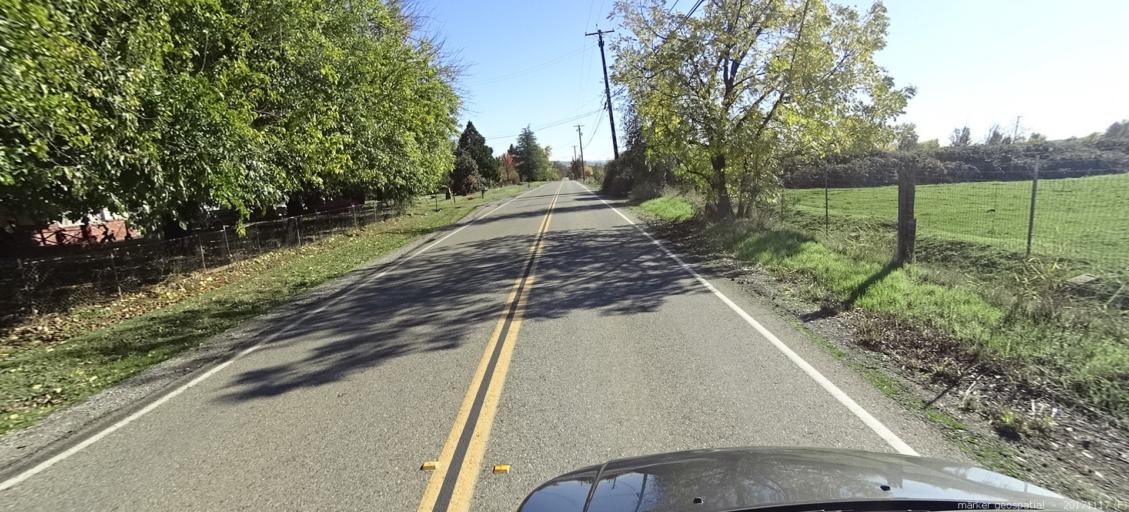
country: US
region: California
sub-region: Shasta County
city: Cottonwood
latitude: 40.4249
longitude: -122.2233
